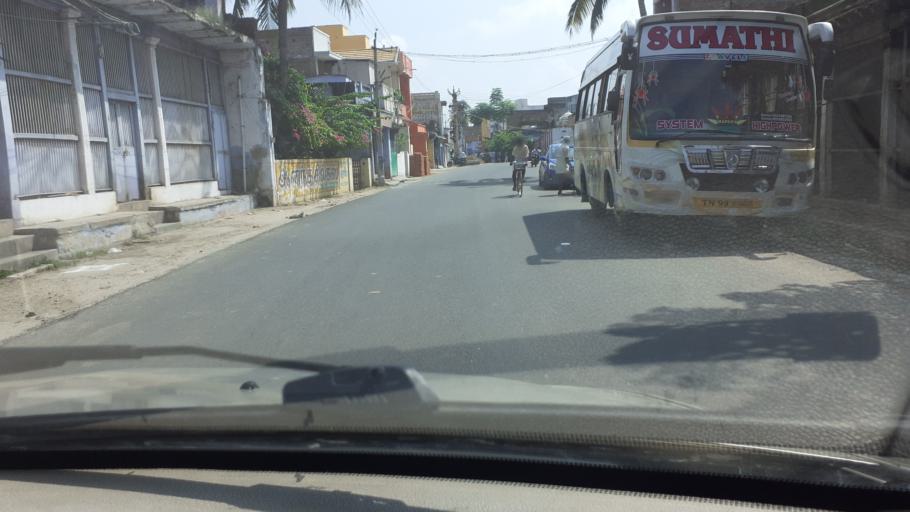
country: IN
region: Tamil Nadu
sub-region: Thoothukkudi
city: Alwar Tirunagari
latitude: 8.6081
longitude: 77.9399
